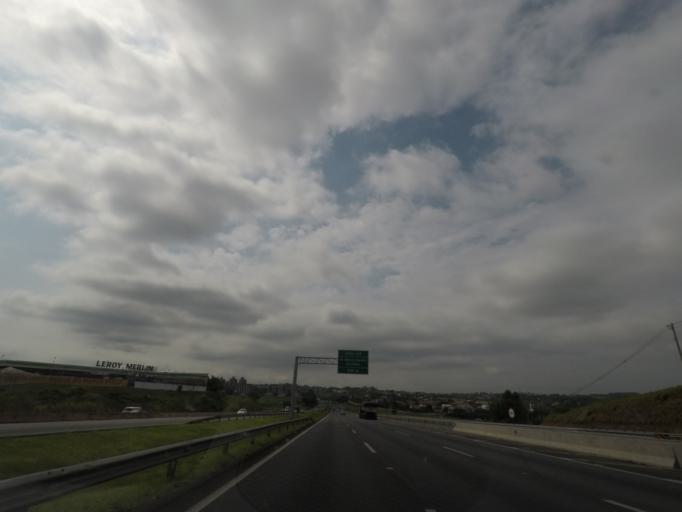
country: BR
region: Sao Paulo
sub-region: Campinas
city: Campinas
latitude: -22.8819
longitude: -47.0143
